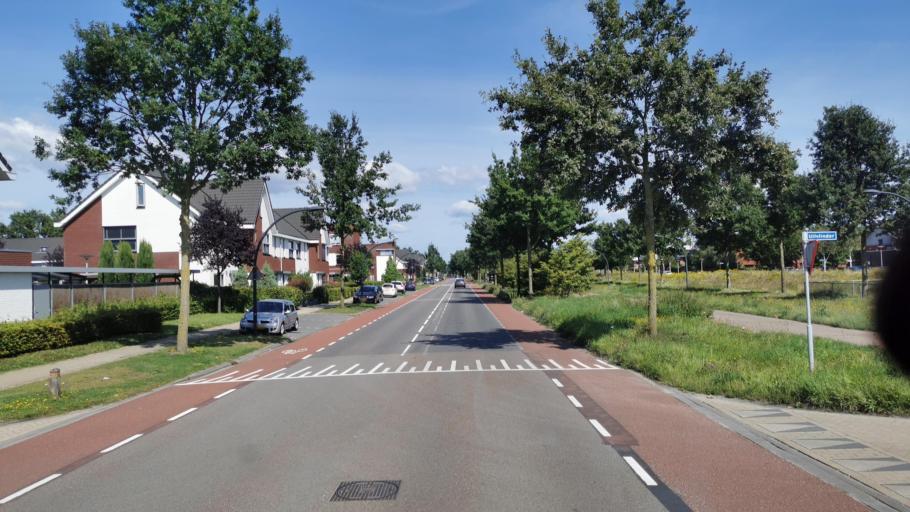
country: DE
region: North Rhine-Westphalia
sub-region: Regierungsbezirk Munster
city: Gronau
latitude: 52.2098
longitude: 6.9609
